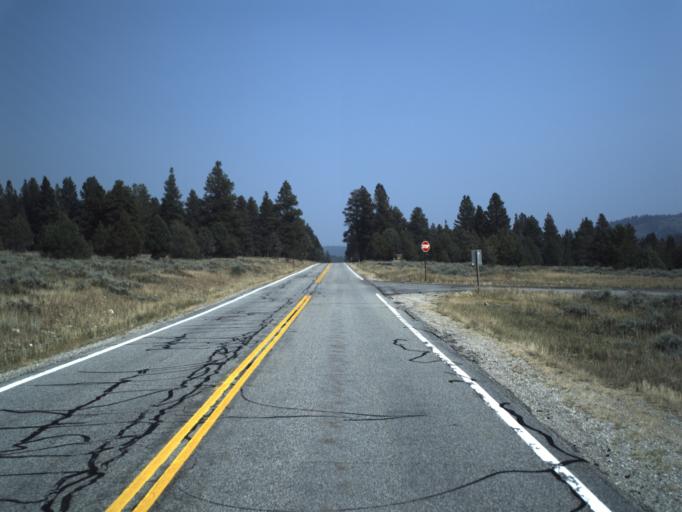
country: US
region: Utah
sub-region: Summit County
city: Kamas
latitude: 40.6307
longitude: -111.1823
